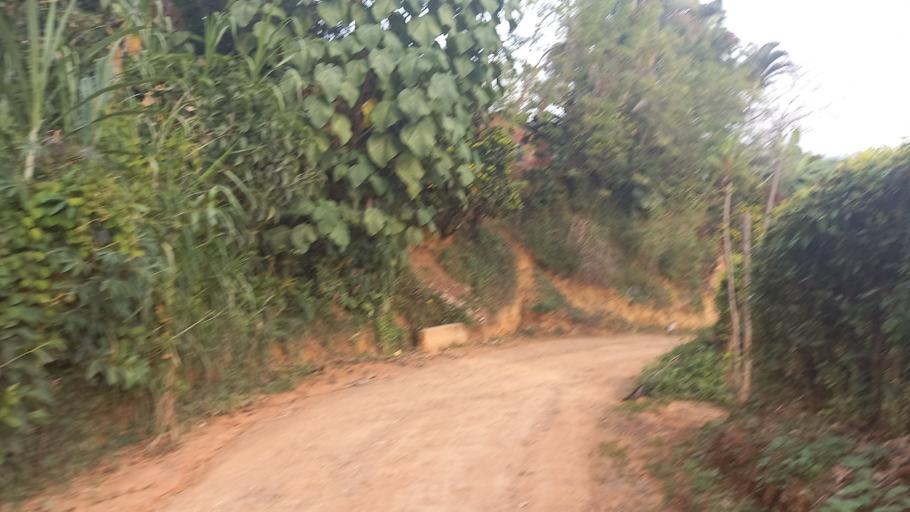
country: CO
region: Antioquia
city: Santa Barbara
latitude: 5.8222
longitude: -75.5751
